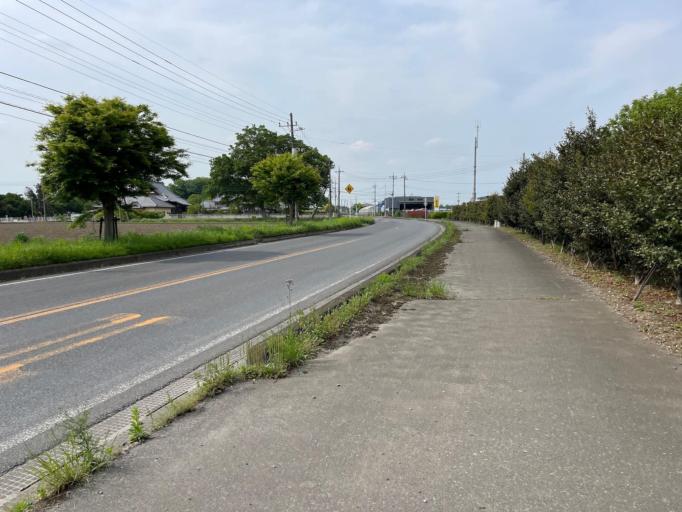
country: JP
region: Tochigi
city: Mibu
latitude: 36.3841
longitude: 139.8046
